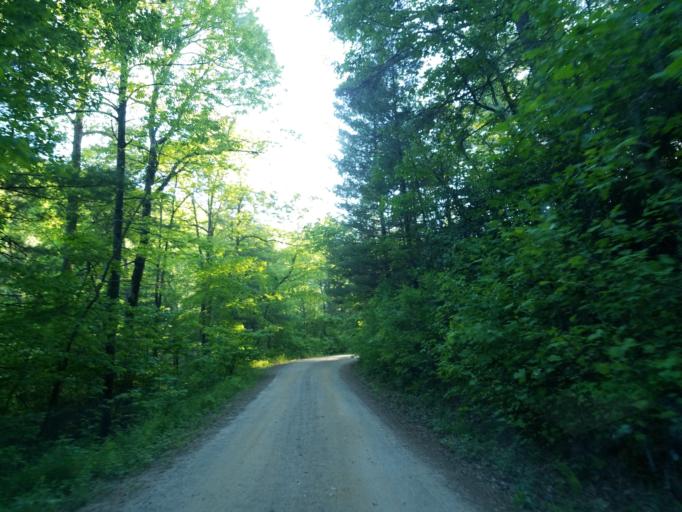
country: US
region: Georgia
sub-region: Lumpkin County
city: Dahlonega
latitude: 34.6801
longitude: -84.1345
